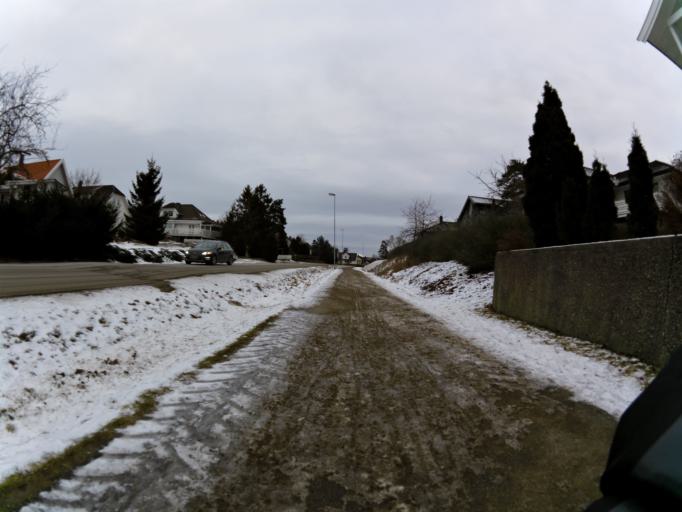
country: NO
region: Ostfold
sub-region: Fredrikstad
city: Fredrikstad
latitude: 59.1966
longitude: 10.8742
